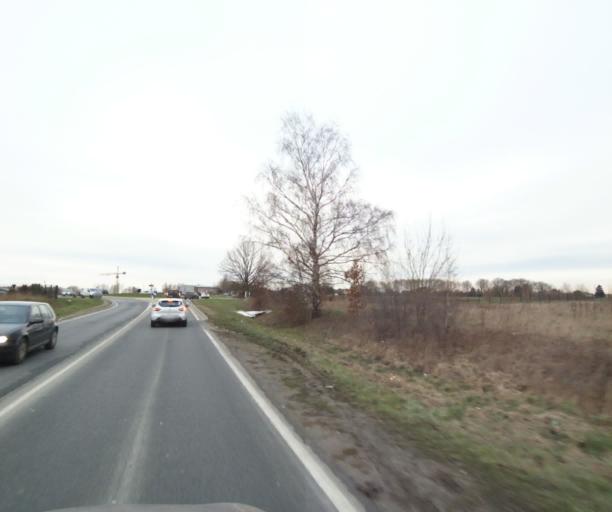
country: FR
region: Ile-de-France
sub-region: Departement de Seine-et-Marne
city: Othis
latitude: 49.0679
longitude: 2.6817
